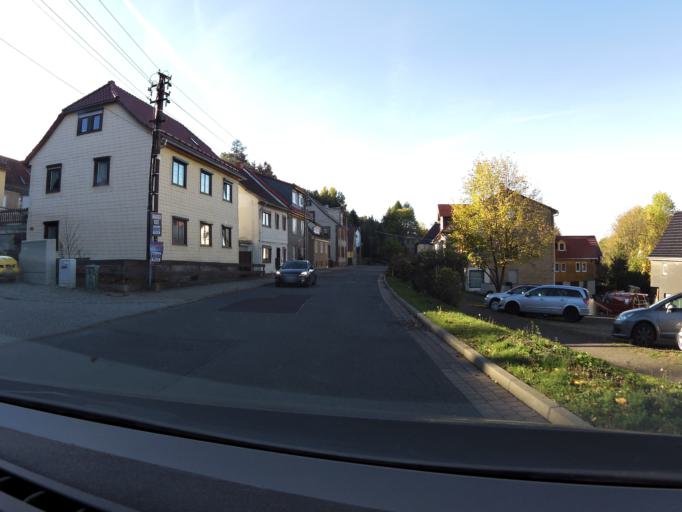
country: DE
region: Thuringia
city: Elgersburg
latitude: 50.7049
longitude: 10.8522
